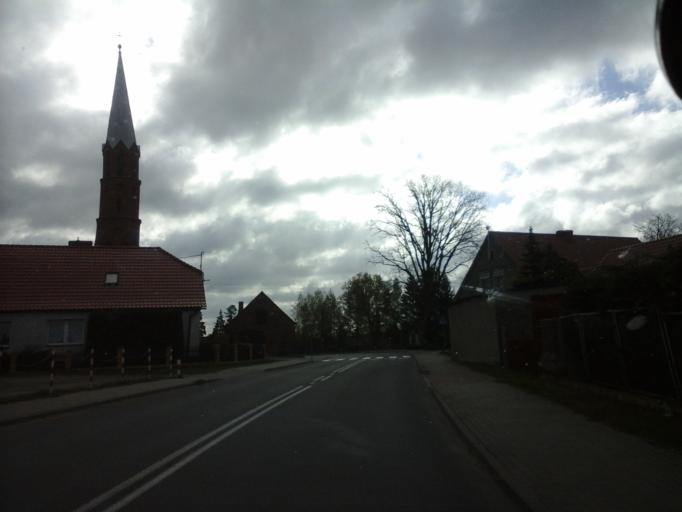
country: PL
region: West Pomeranian Voivodeship
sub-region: Powiat choszczenski
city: Krzecin
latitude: 53.1414
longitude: 15.5023
